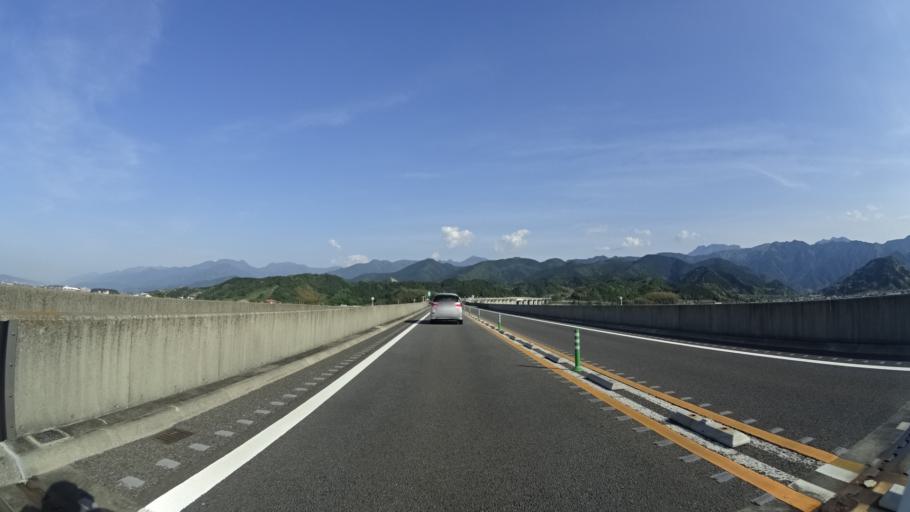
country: JP
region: Ehime
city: Saijo
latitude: 33.8948
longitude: 133.0811
